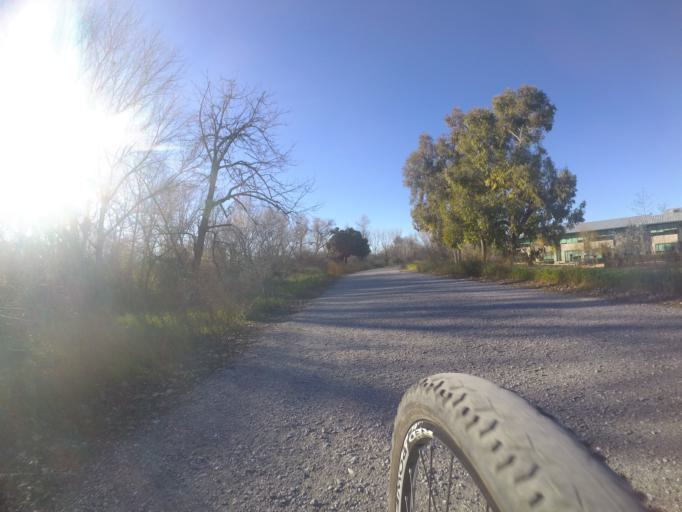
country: US
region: California
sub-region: Santa Clara County
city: Milpitas
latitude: 37.4129
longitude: -121.9246
